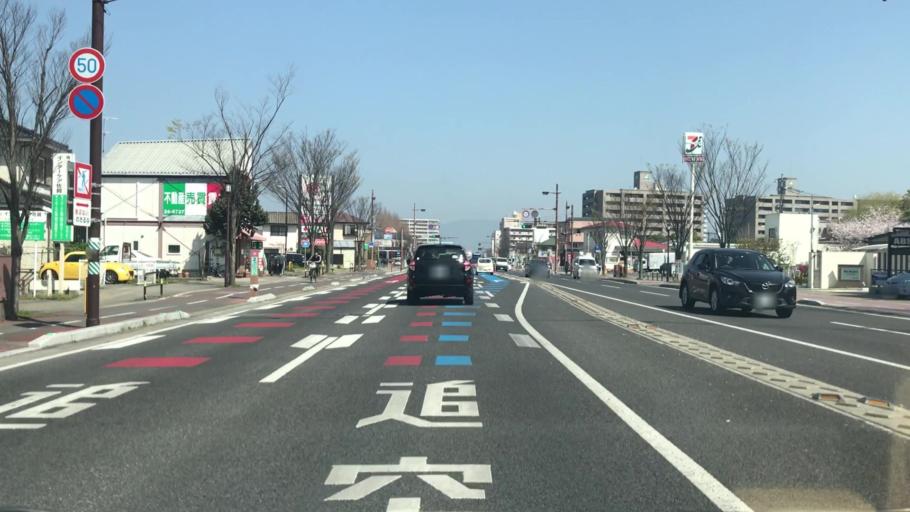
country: JP
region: Saga Prefecture
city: Saga-shi
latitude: 33.2564
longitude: 130.2929
